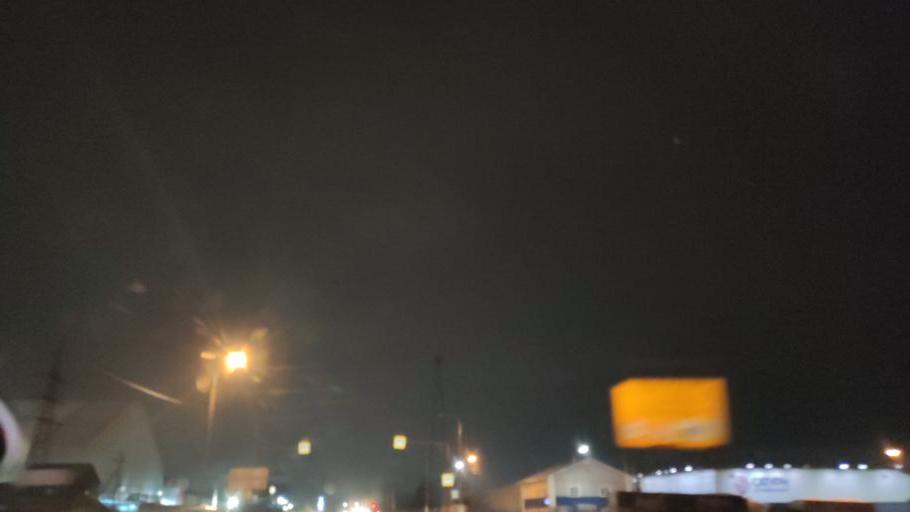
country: RU
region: Moskovskaya
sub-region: Podol'skiy Rayon
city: Podol'sk
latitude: 55.4360
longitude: 37.6048
